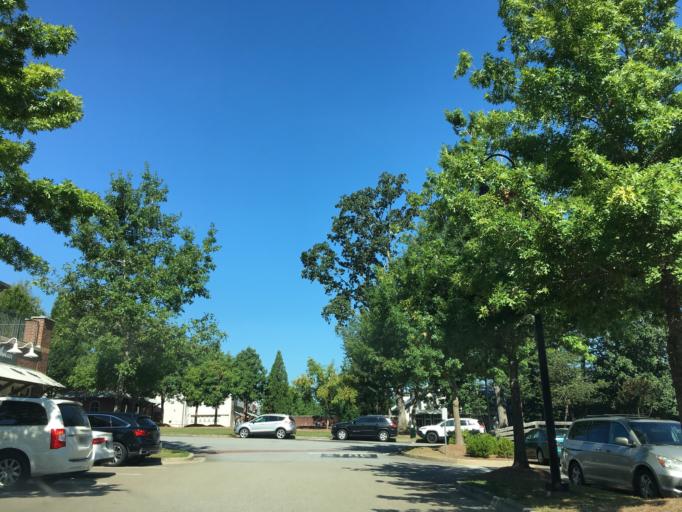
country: US
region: Georgia
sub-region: Fulton County
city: Milton
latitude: 34.1664
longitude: -84.3310
